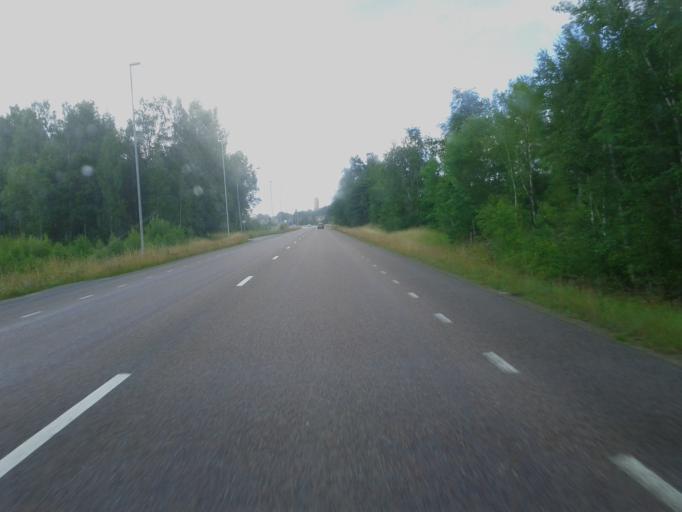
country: SE
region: Vaestmanland
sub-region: Sala Kommun
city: Sala
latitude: 59.9047
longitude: 16.5806
